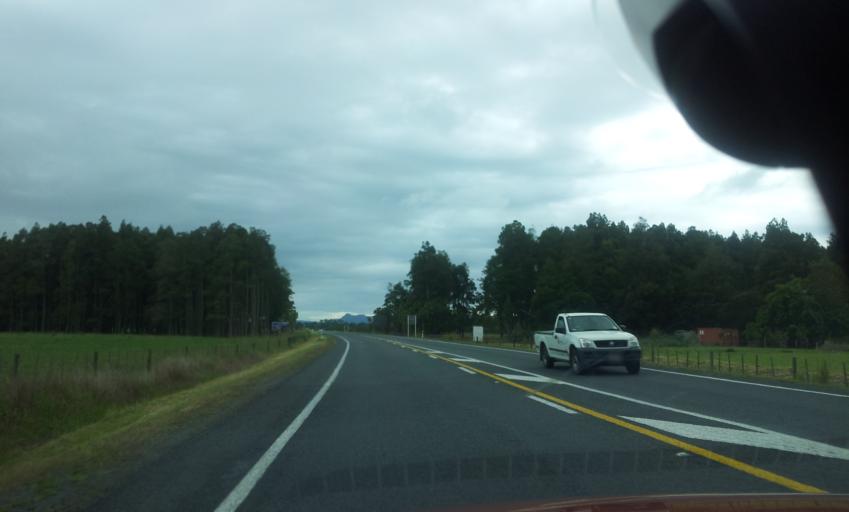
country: NZ
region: Northland
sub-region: Whangarei
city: Ruakaka
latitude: -35.9848
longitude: 174.4301
